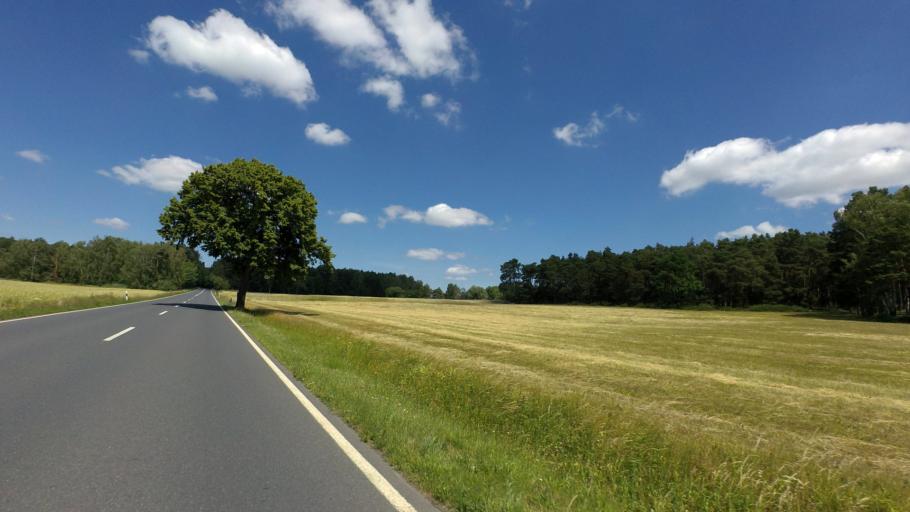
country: DE
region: Brandenburg
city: Luckau
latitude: 51.8880
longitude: 13.6867
